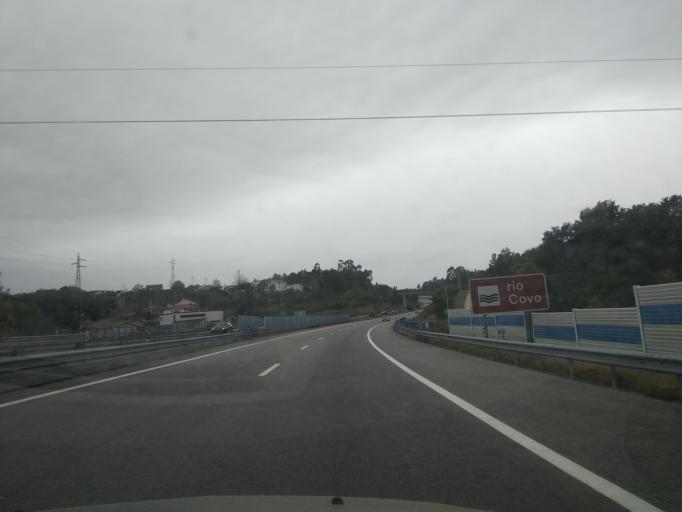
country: PT
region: Braga
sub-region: Barcelos
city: Barcelos
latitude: 41.5247
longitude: -8.5867
